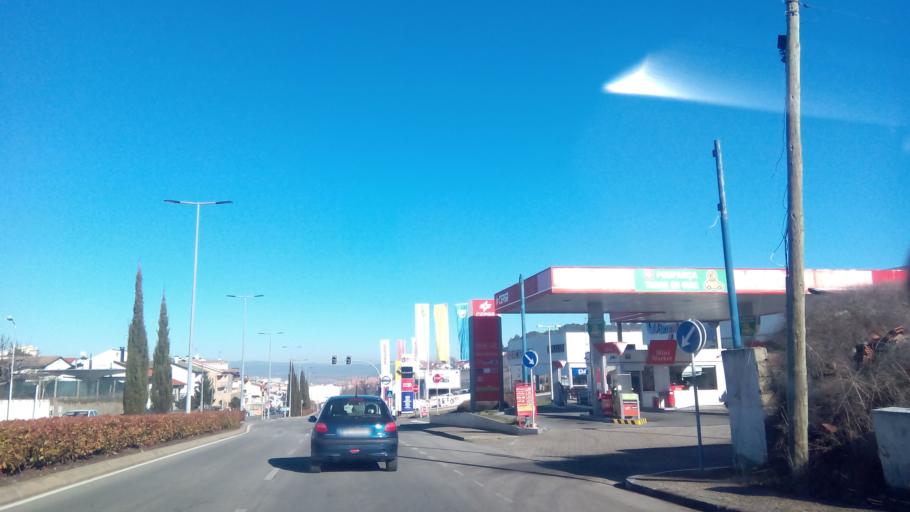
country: PT
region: Braganca
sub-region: Braganca Municipality
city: Braganca
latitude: 41.7863
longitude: -6.7745
